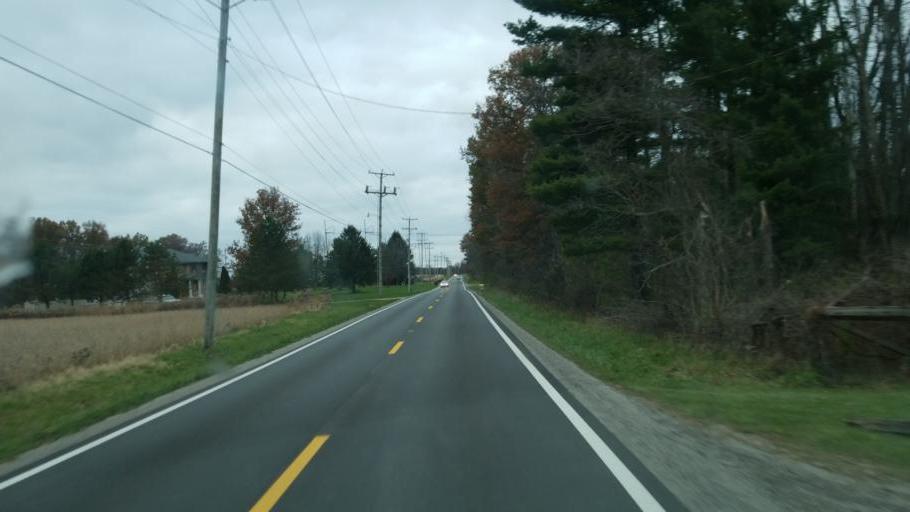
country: US
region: Ohio
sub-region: Franklin County
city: New Albany
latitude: 40.1194
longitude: -82.8399
